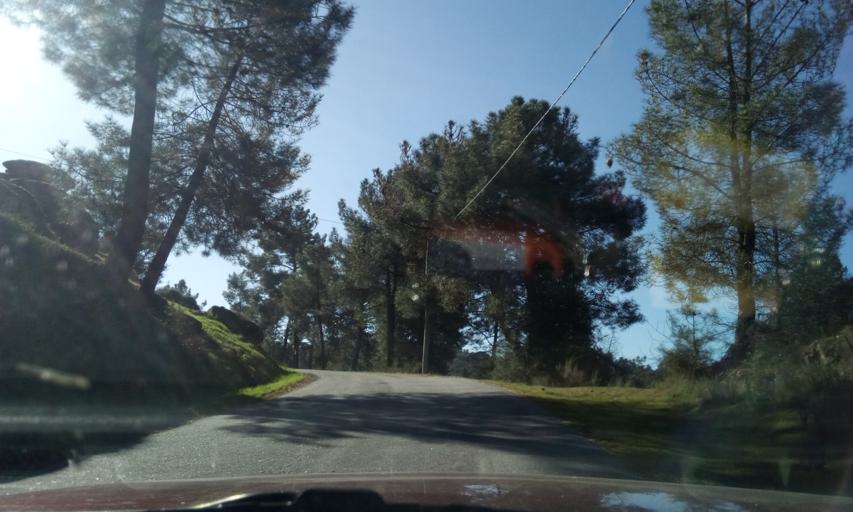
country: PT
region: Guarda
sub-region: Celorico da Beira
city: Celorico da Beira
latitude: 40.6844
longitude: -7.3982
